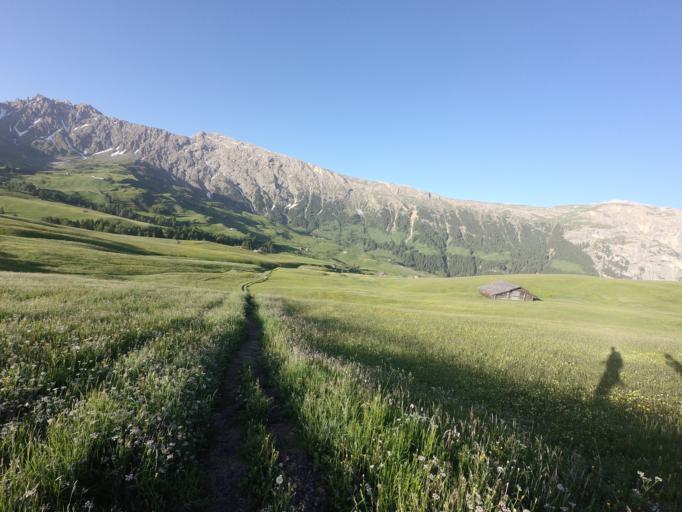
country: IT
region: Trentino-Alto Adige
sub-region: Bolzano
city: Siusi
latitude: 46.5250
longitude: 11.6177
